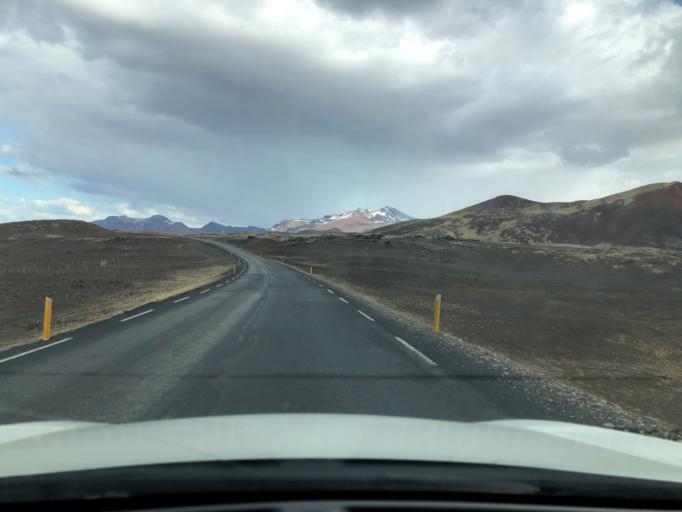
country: IS
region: West
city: Stykkisholmur
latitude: 64.9647
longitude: -22.9792
